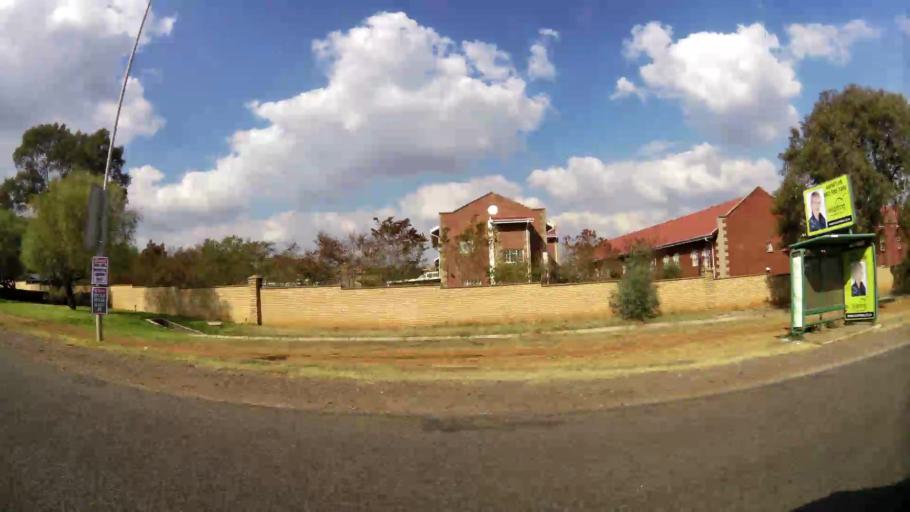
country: ZA
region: Gauteng
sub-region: City of Tshwane Metropolitan Municipality
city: Centurion
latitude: -25.8696
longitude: 28.2349
